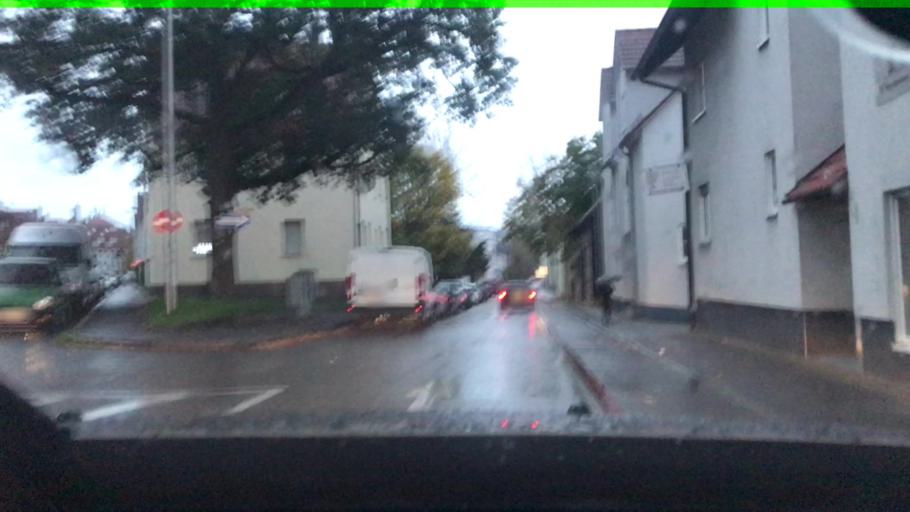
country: DE
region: Baden-Wuerttemberg
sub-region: Regierungsbezirk Stuttgart
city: Winnenden
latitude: 48.8772
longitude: 9.3930
